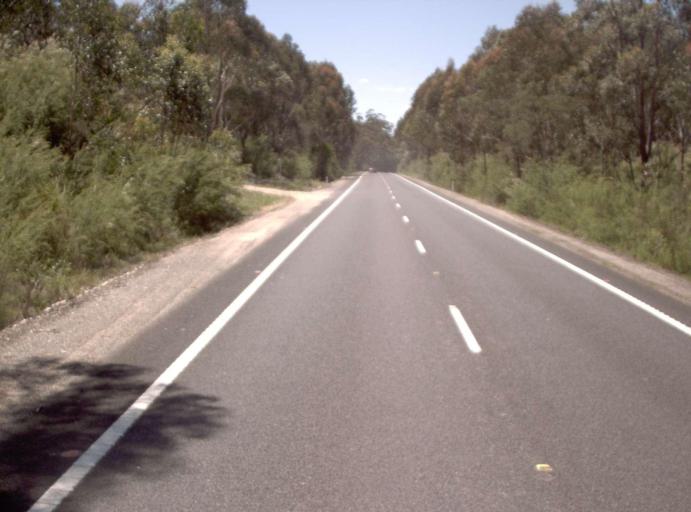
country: AU
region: Victoria
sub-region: East Gippsland
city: Lakes Entrance
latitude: -37.6949
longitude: 148.6128
